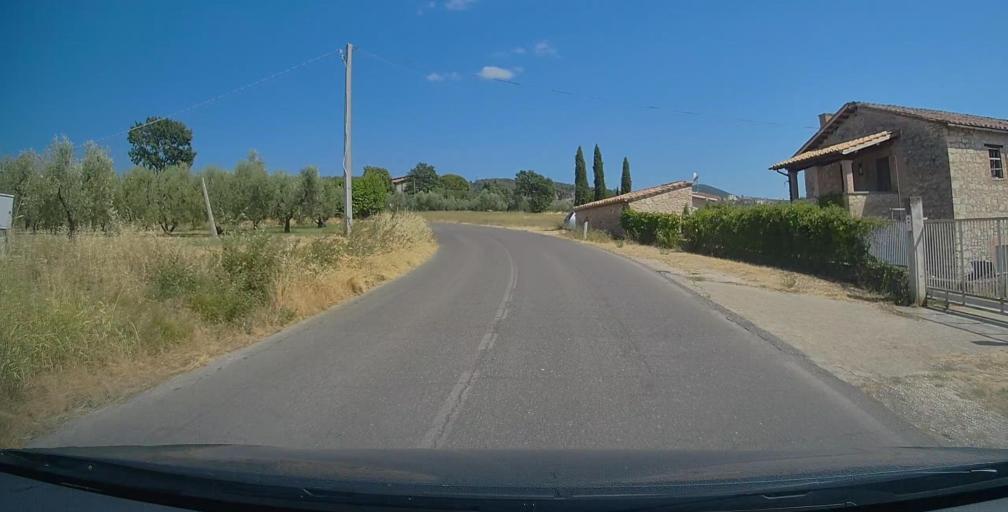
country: IT
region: Umbria
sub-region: Provincia di Terni
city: Calvi dell'Umbria
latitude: 42.4123
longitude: 12.5526
